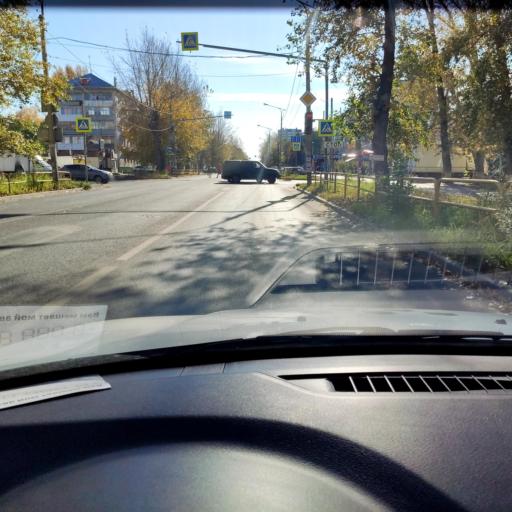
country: RU
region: Samara
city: Tol'yatti
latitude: 53.5335
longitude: 49.4110
